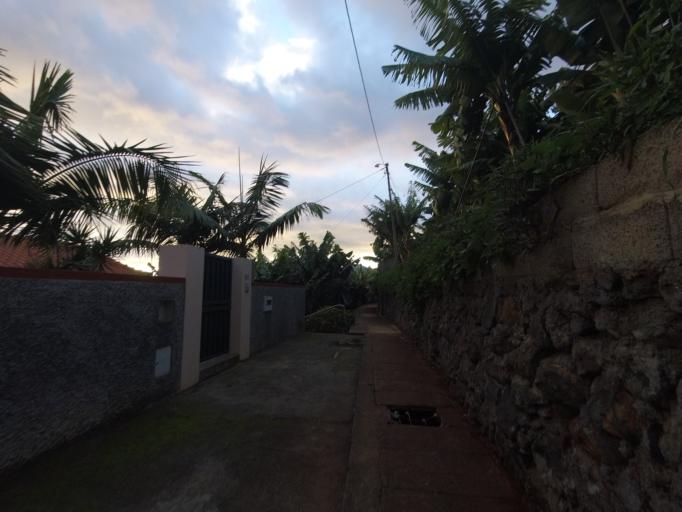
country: PT
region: Madeira
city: Camara de Lobos
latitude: 32.6619
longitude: -16.9550
